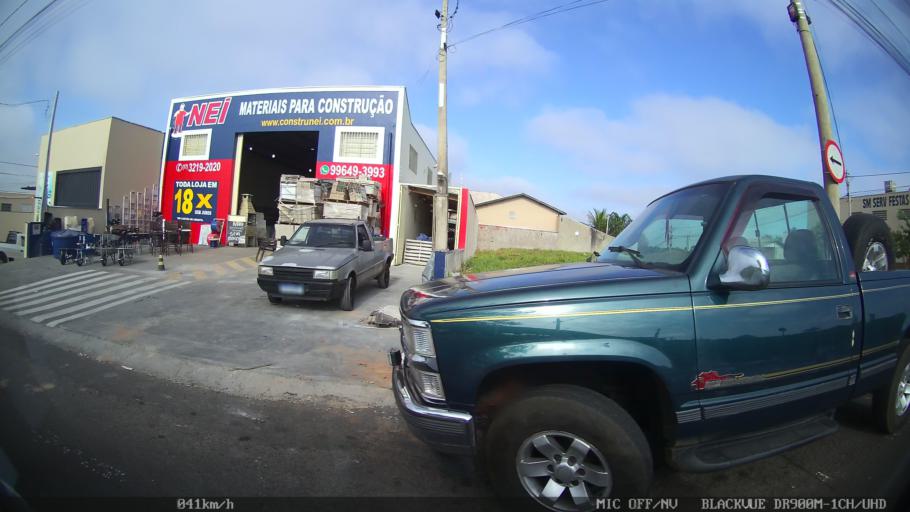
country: BR
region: Sao Paulo
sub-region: Sao Jose Do Rio Preto
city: Sao Jose do Rio Preto
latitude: -20.8018
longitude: -49.4306
